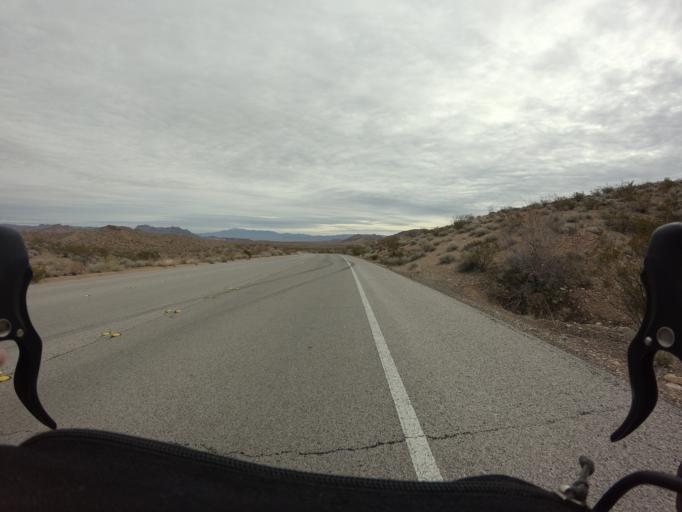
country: US
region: Nevada
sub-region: Clark County
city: Boulder City
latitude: 36.2282
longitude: -114.6115
